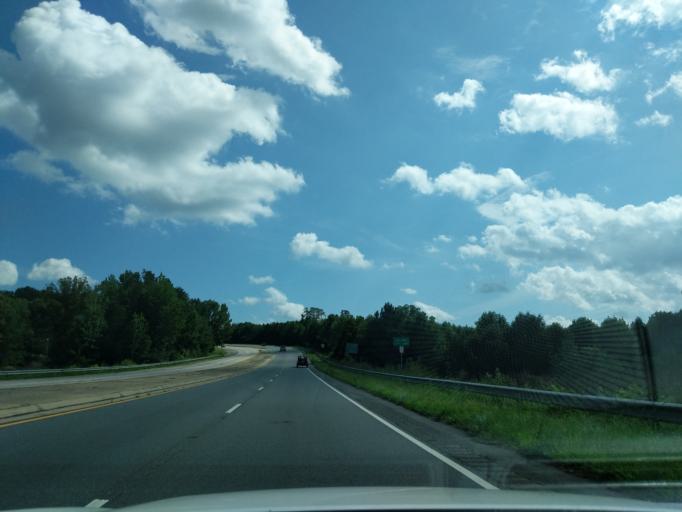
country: US
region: Georgia
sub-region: Habersham County
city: Baldwin
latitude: 34.5058
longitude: -83.5455
